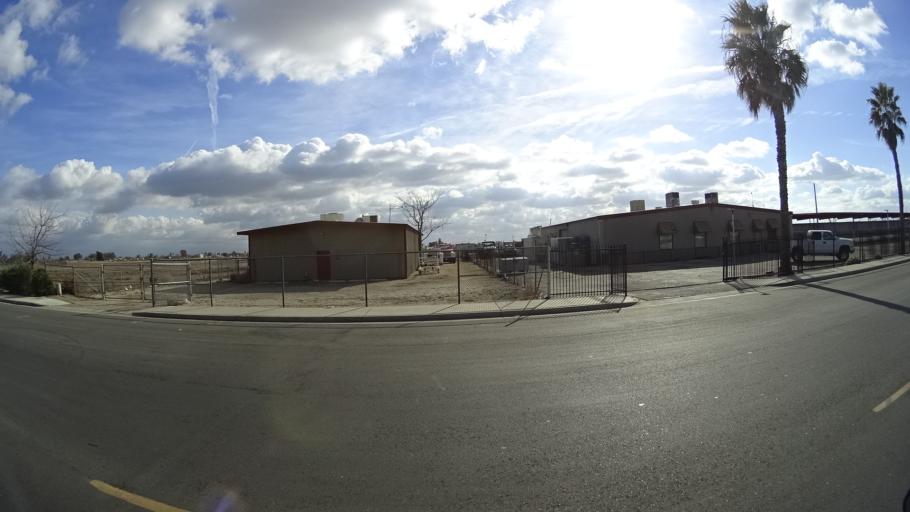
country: US
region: California
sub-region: Kern County
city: Bakersfield
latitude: 35.3323
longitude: -118.9982
